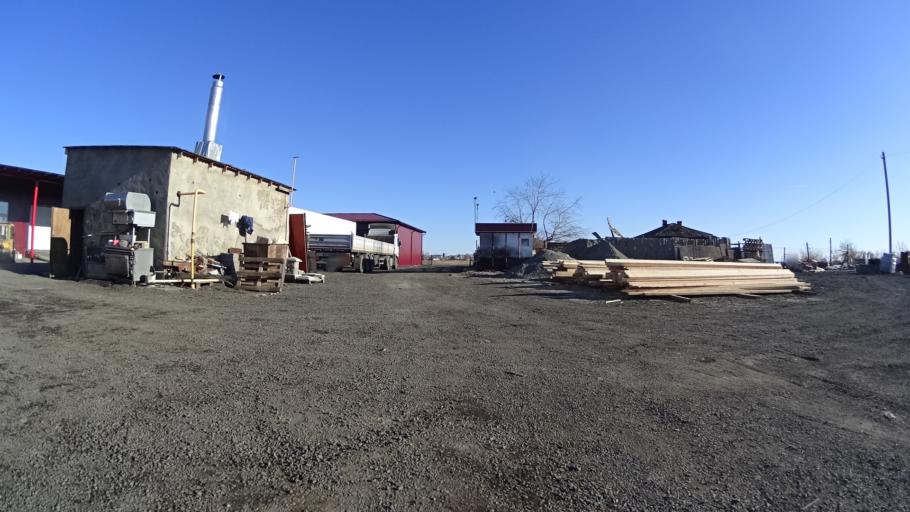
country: RU
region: Chelyabinsk
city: Troitsk
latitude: 54.0827
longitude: 61.5112
